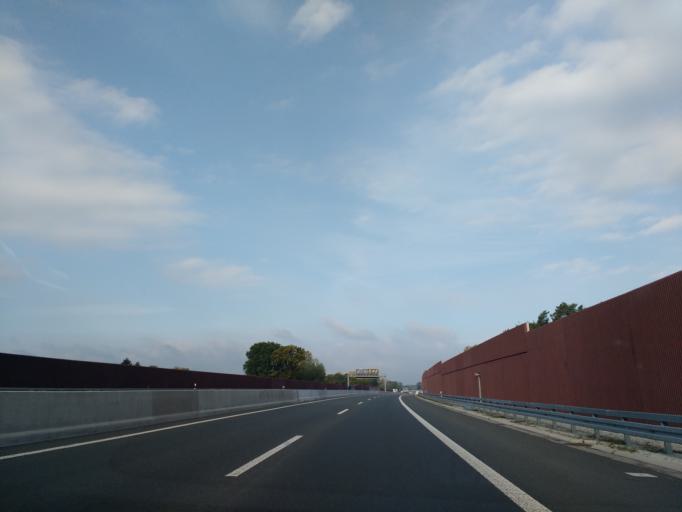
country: DE
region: North Rhine-Westphalia
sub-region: Regierungsbezirk Detmold
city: Steinhagen
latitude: 51.9780
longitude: 8.4670
